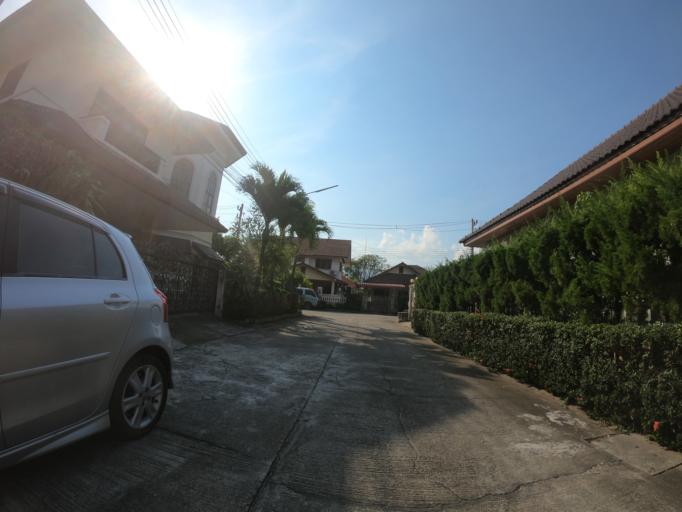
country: TH
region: Chiang Mai
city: Chiang Mai
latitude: 18.8241
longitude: 99.0024
